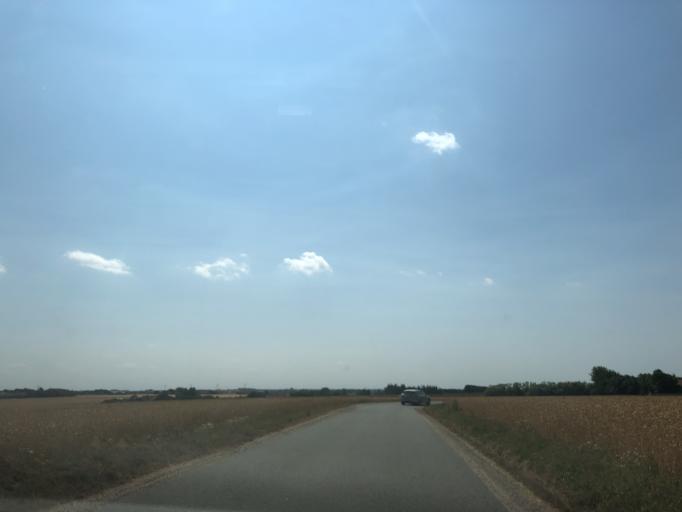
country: DK
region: North Denmark
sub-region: Morso Kommune
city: Nykobing Mors
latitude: 56.8223
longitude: 8.9937
